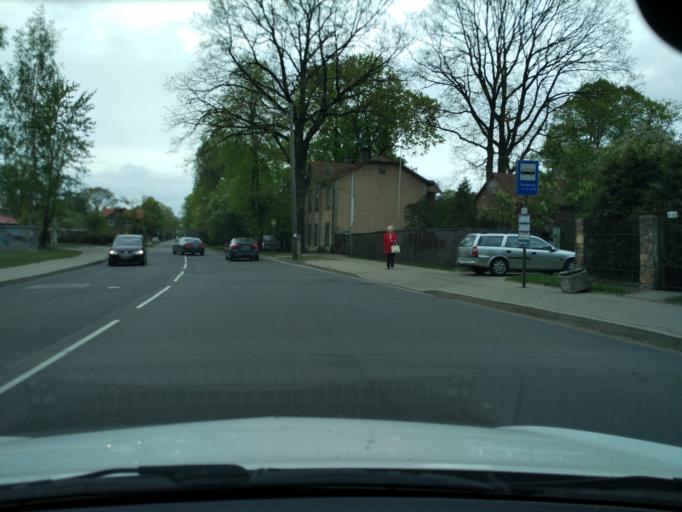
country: LV
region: Marupe
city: Marupe
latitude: 56.9170
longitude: 24.0732
